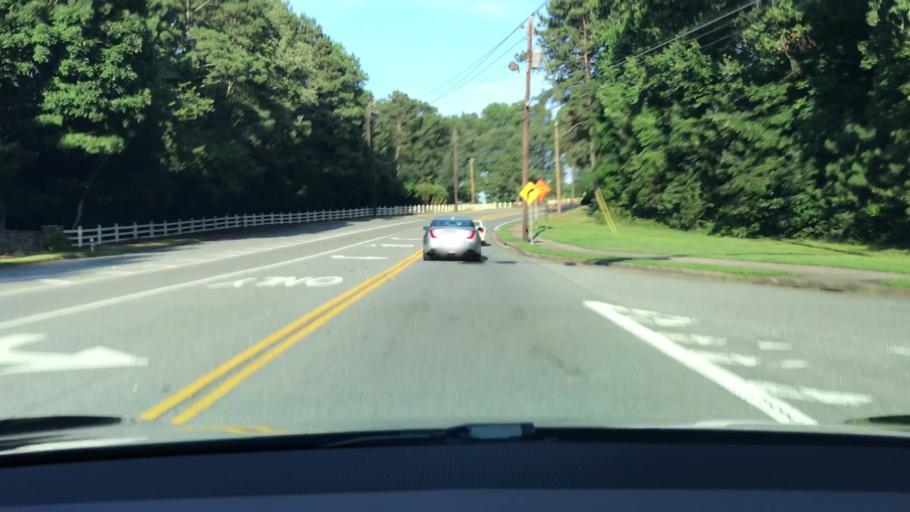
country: US
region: Georgia
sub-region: Fulton County
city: Alpharetta
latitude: 34.0757
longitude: -84.2394
